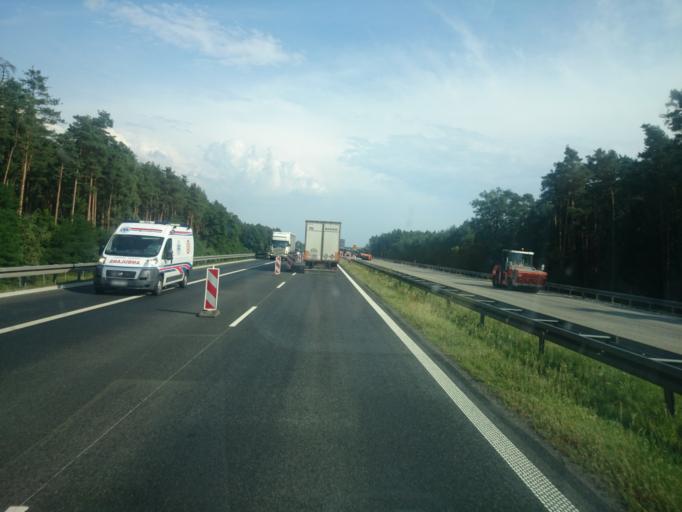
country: PL
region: Opole Voivodeship
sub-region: Powiat opolski
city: Dabrowa
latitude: 50.6206
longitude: 17.7619
